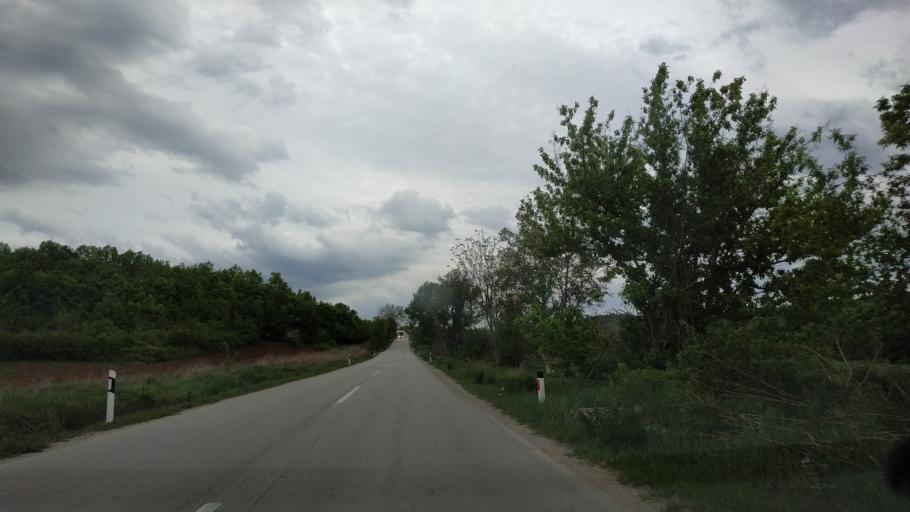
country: RS
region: Central Serbia
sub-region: Nisavski Okrug
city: Aleksinac
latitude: 43.6144
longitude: 21.6900
